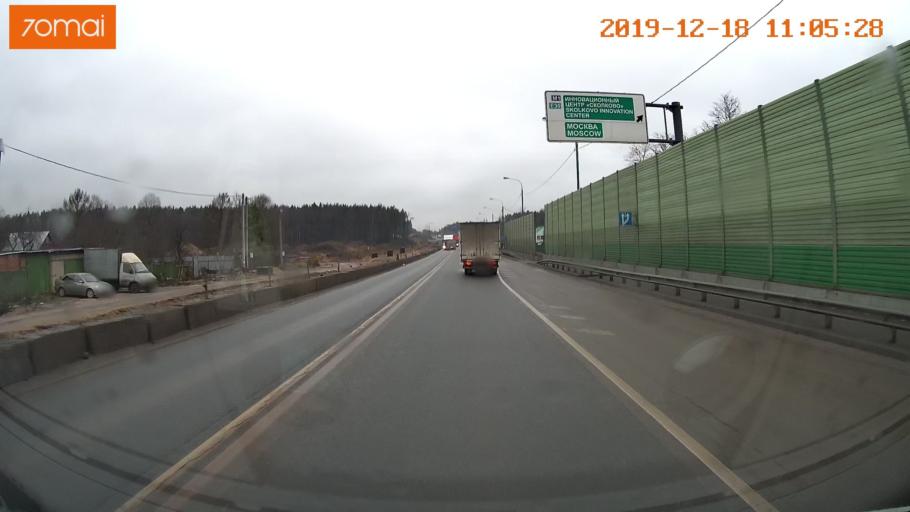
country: RU
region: Moskovskaya
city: Golitsyno
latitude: 55.5982
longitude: 37.0077
